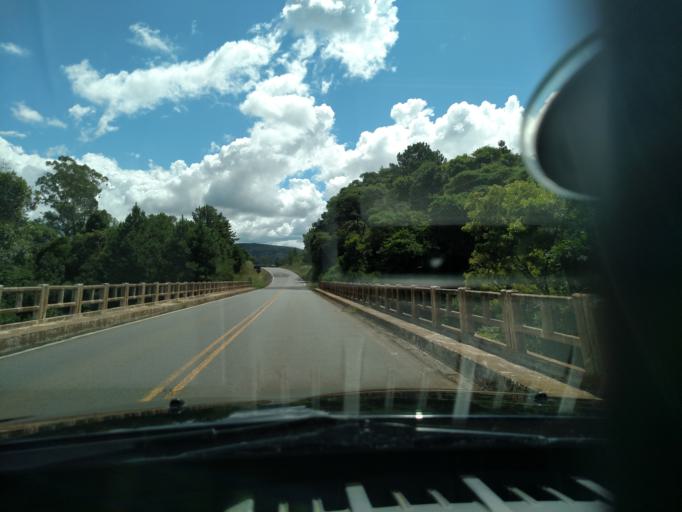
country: BR
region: Santa Catarina
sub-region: Lages
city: Lages
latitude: -27.8658
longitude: -50.2034
